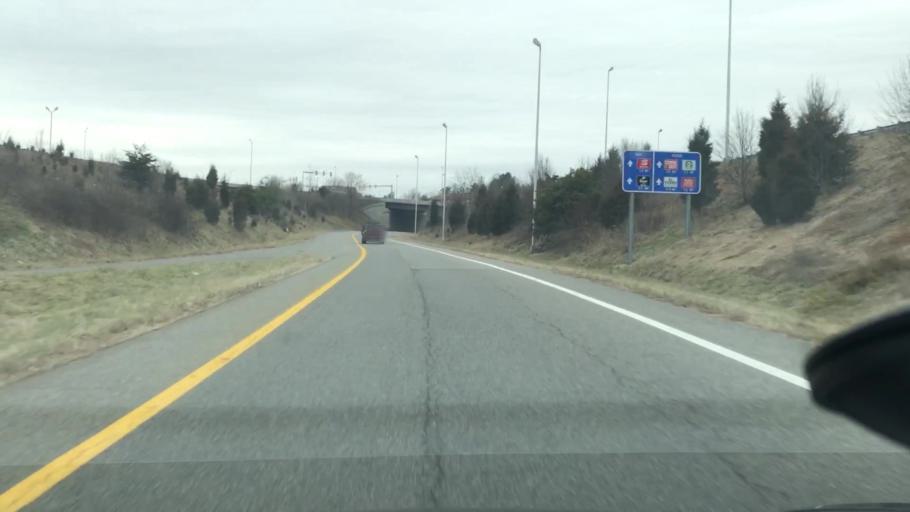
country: US
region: Virginia
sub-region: Montgomery County
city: Merrimac
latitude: 37.1922
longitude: -80.4006
